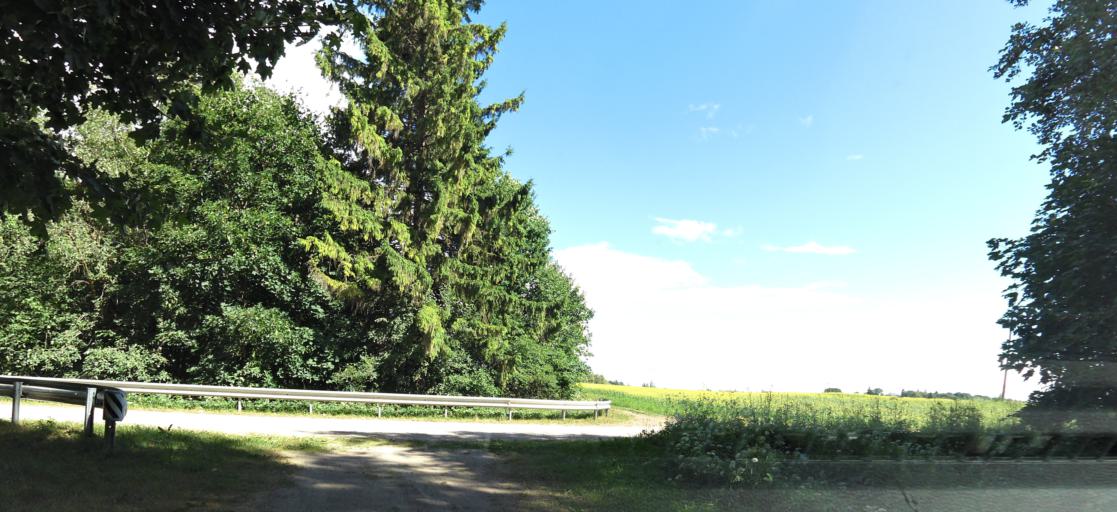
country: LT
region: Panevezys
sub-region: Birzai
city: Birzai
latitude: 56.3507
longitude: 24.6307
